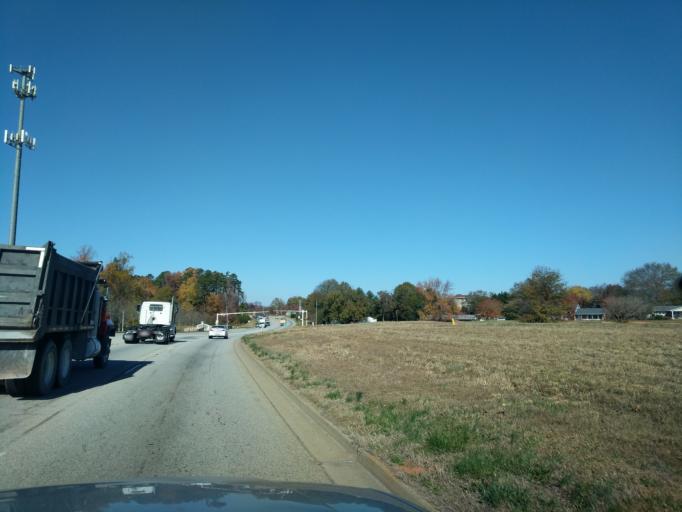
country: US
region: South Carolina
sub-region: Greenville County
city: Greer
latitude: 34.9213
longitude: -82.2429
